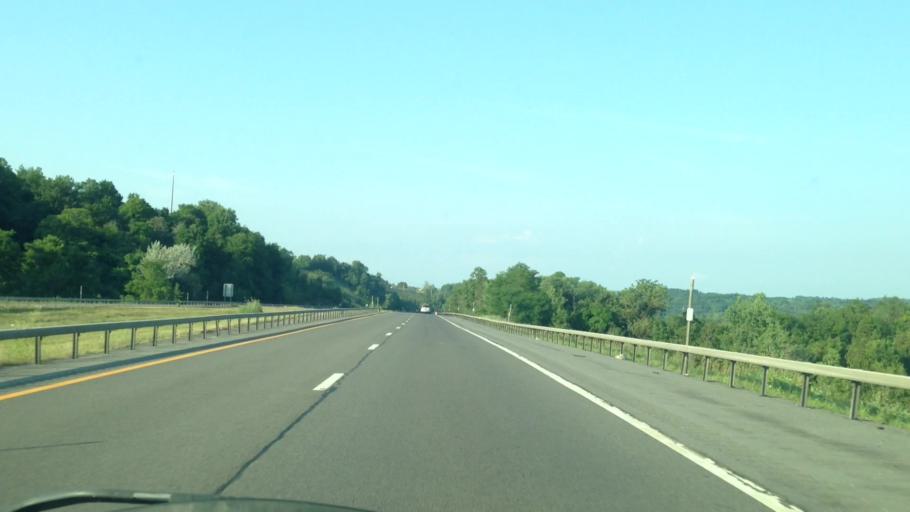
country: US
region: New York
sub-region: Onondaga County
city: Nedrow
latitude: 43.0049
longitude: -76.0916
